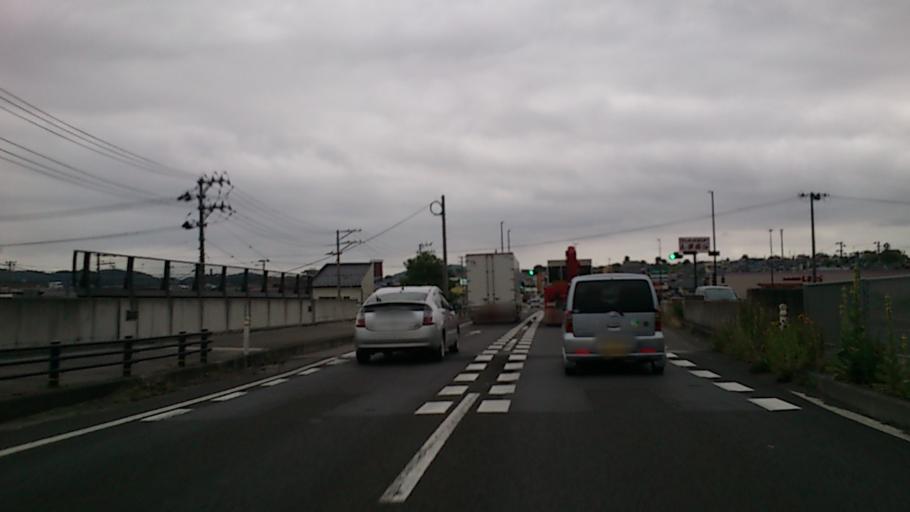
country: JP
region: Fukushima
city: Motomiya
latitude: 37.5201
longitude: 140.3955
